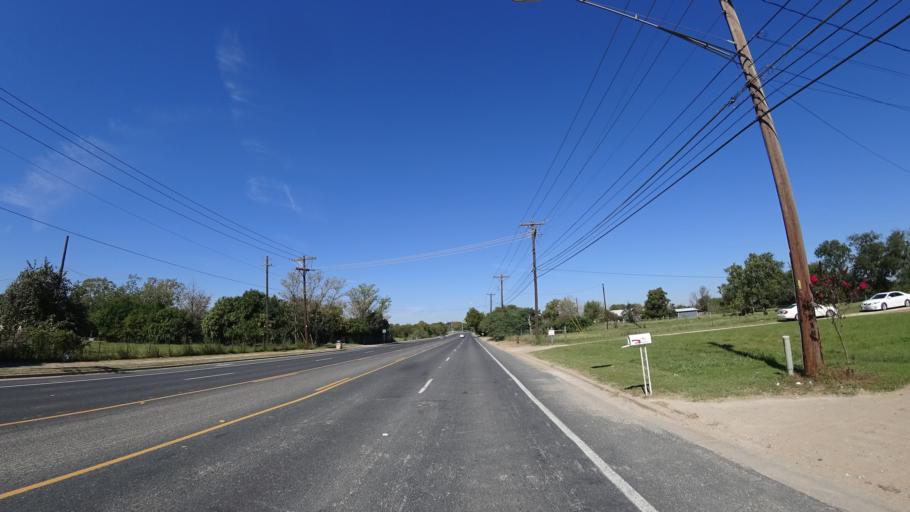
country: US
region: Texas
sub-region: Travis County
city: Austin
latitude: 30.1881
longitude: -97.6941
